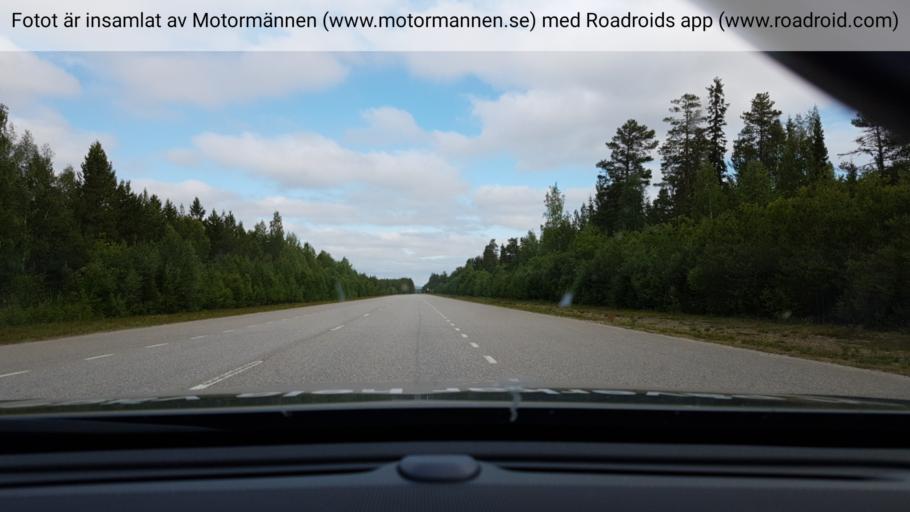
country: SE
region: Vaesterbotten
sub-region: Norsjo Kommun
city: Norsjoe
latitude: 64.5707
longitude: 19.3107
